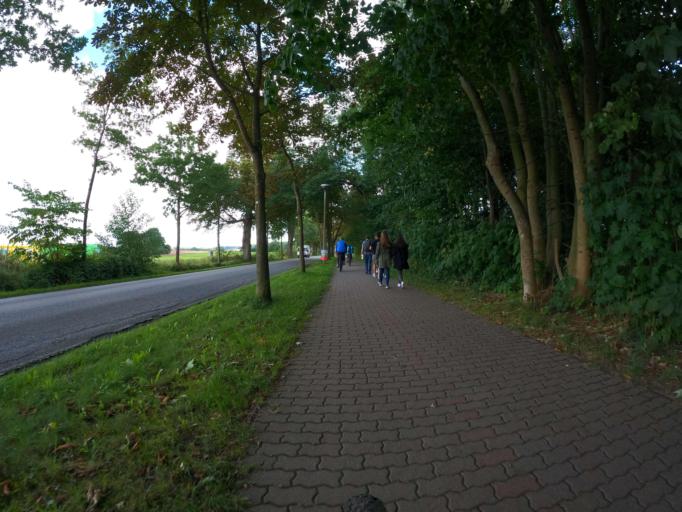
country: DE
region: Mecklenburg-Vorpommern
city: Putbus
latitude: 54.3478
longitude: 13.4909
